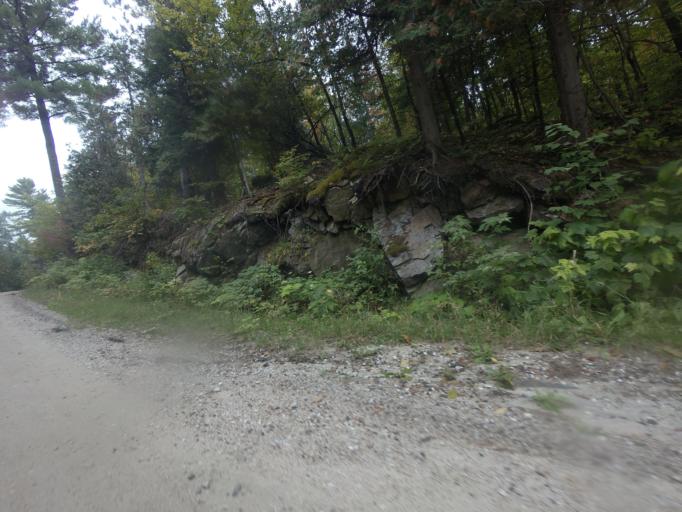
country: CA
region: Quebec
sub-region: Outaouais
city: Maniwaki
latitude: 46.0321
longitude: -75.9391
